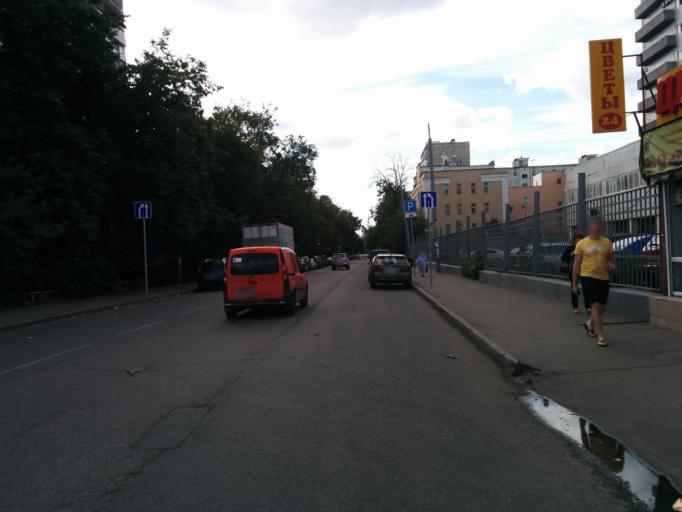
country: RU
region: Moscow
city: Mar'ina Roshcha
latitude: 55.7926
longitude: 37.6131
